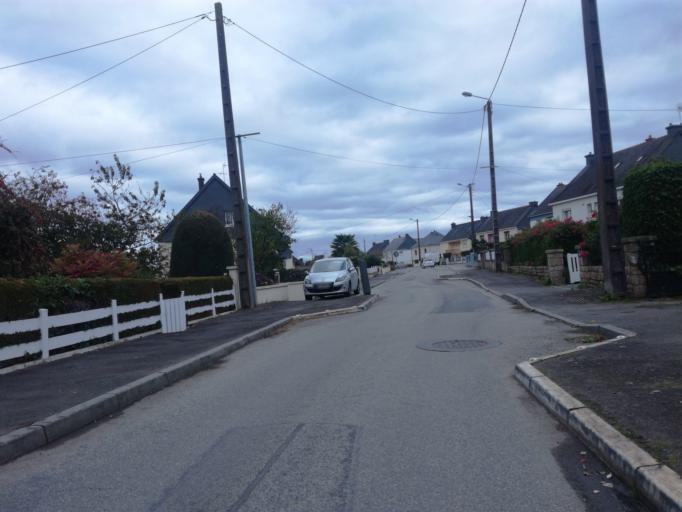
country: FR
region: Brittany
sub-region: Departement du Morbihan
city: Le Sourn
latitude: 48.0415
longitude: -2.9866
